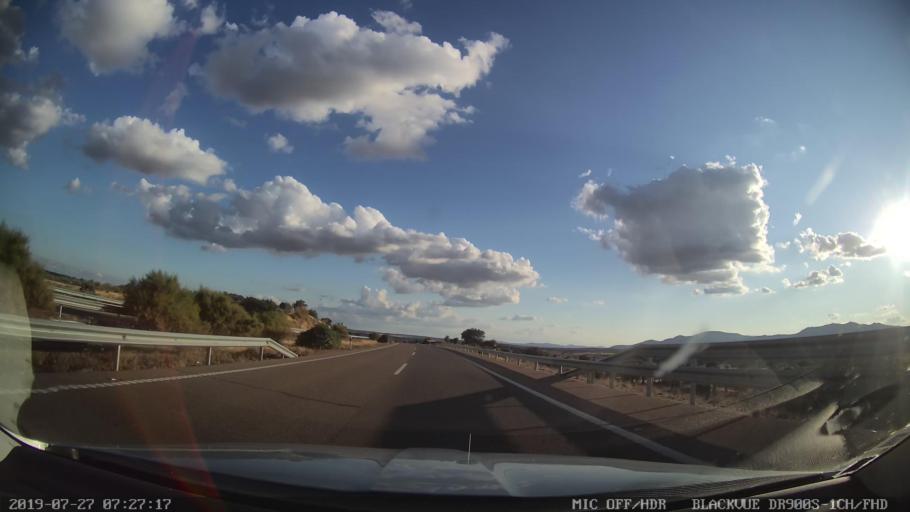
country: ES
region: Extremadura
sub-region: Provincia de Caceres
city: Villamesias
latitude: 39.2489
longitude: -5.8795
